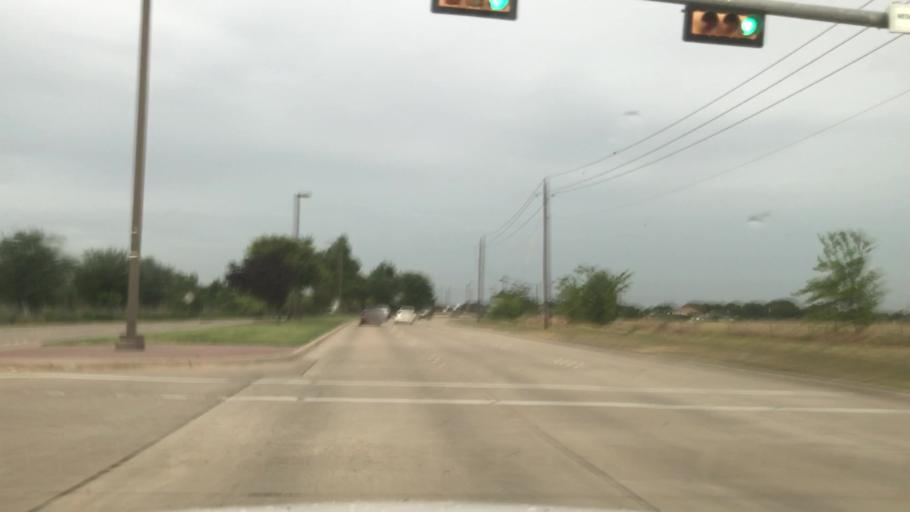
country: US
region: Texas
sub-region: Dallas County
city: Mesquite
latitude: 32.7375
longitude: -96.5660
